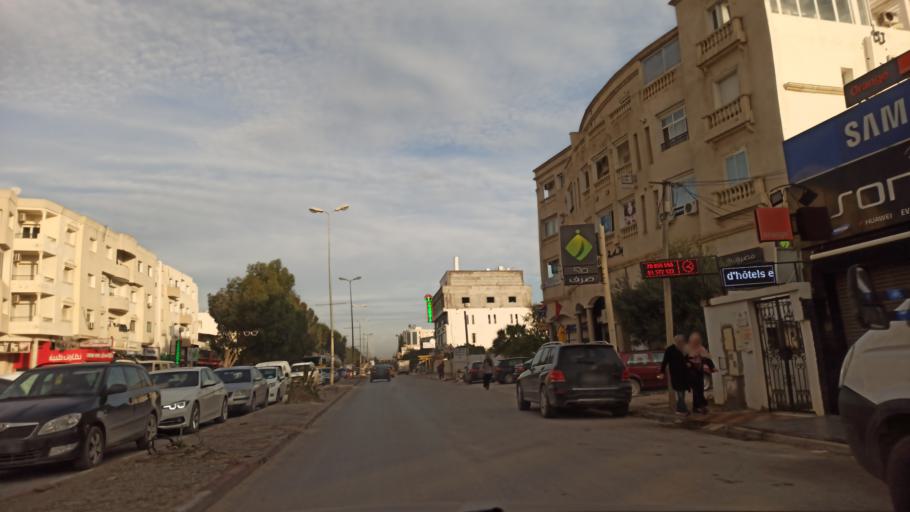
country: TN
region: Tunis
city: La Goulette
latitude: 36.8545
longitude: 10.2574
